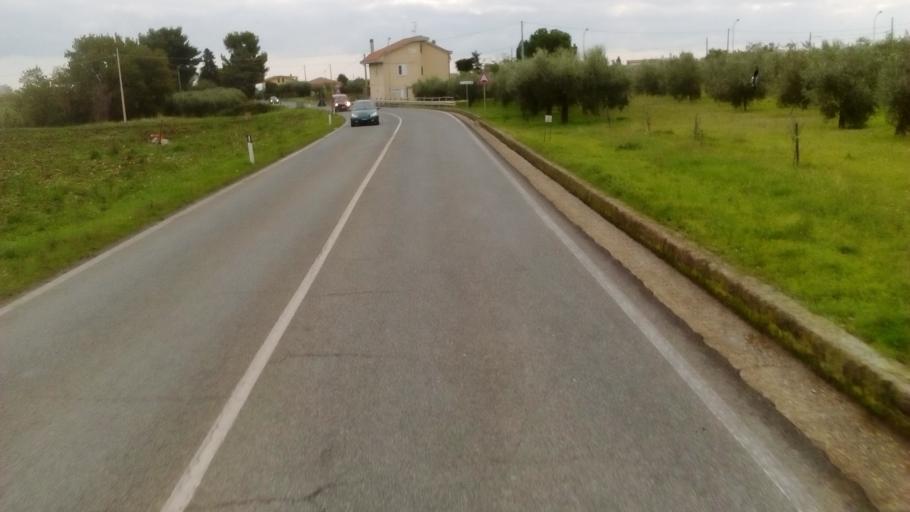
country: IT
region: Abruzzo
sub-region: Provincia di Chieti
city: Vasto
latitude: 42.1650
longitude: 14.6680
